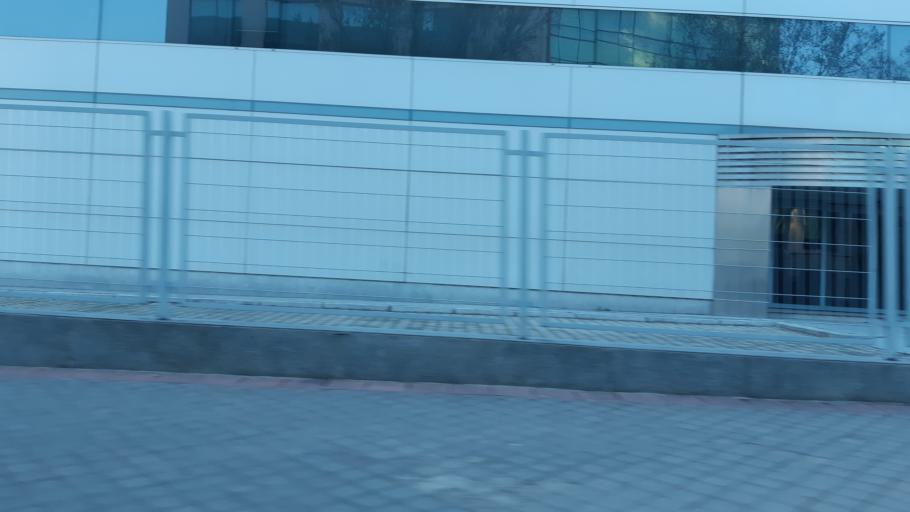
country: ES
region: Madrid
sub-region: Provincia de Madrid
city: San Blas
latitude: 40.4335
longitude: -3.6320
